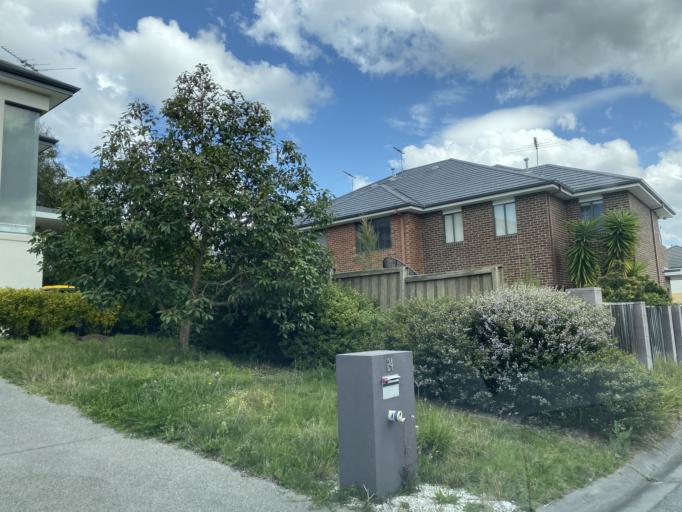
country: AU
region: Victoria
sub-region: Monash
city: Ashwood
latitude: -37.8580
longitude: 145.1107
